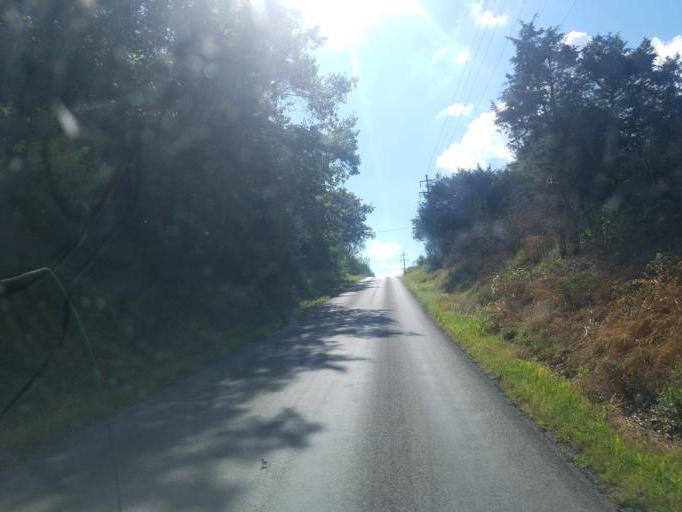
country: US
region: Illinois
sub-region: Jackson County
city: Murphysboro
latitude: 37.7090
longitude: -89.3091
